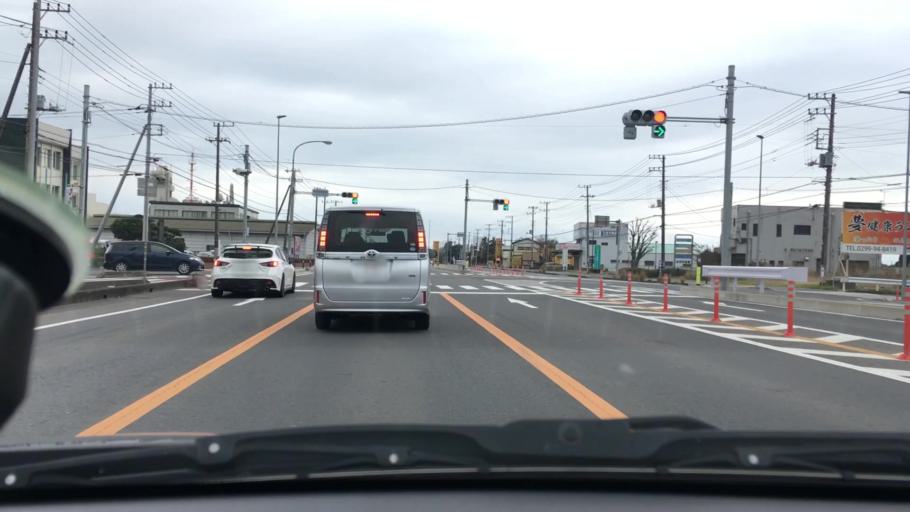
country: JP
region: Chiba
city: Omigawa
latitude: 35.8892
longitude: 140.6646
